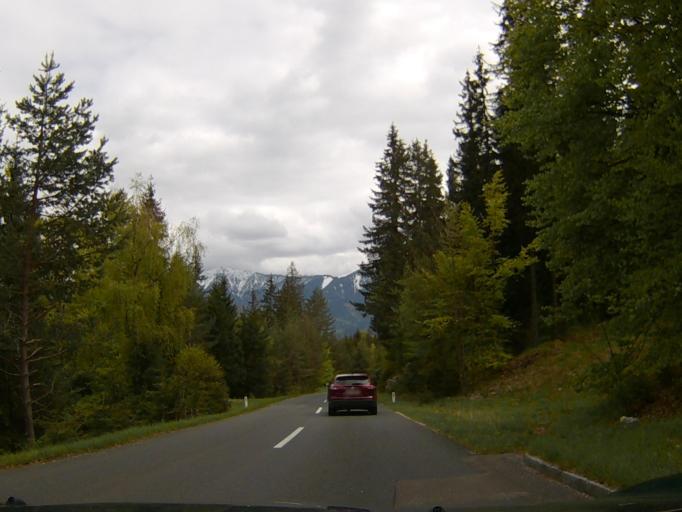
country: AT
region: Carinthia
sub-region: Politischer Bezirk Villach Land
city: Arnoldstein
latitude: 46.5856
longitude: 13.7785
